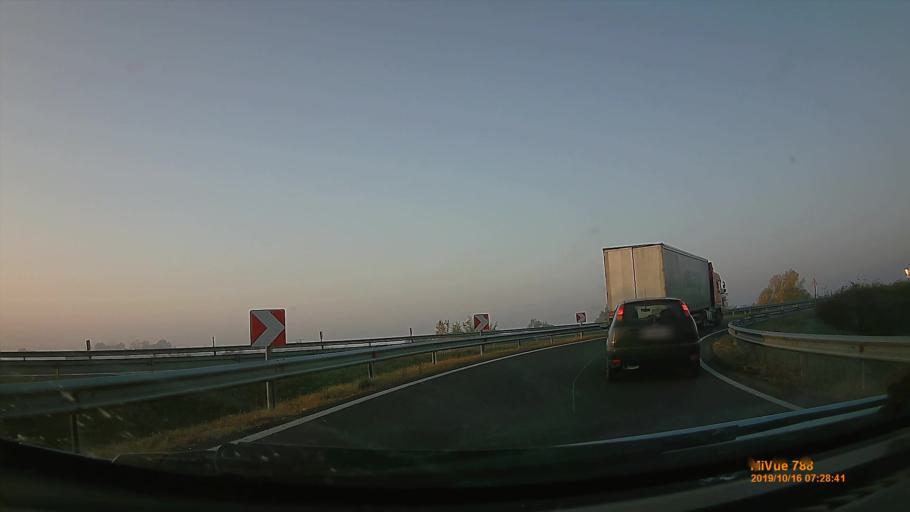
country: HU
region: Heves
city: Fuzesabony
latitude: 47.7300
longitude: 20.4164
